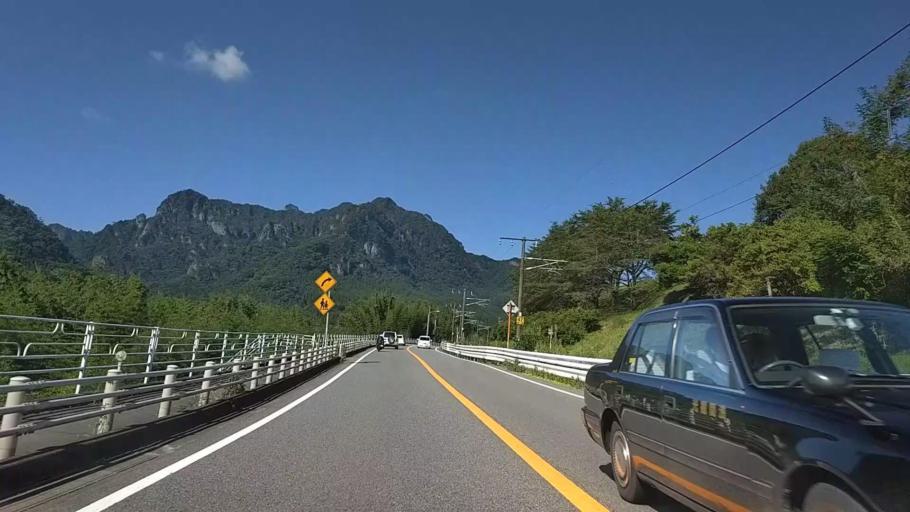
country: JP
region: Gunma
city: Annaka
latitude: 36.3257
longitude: 138.7618
